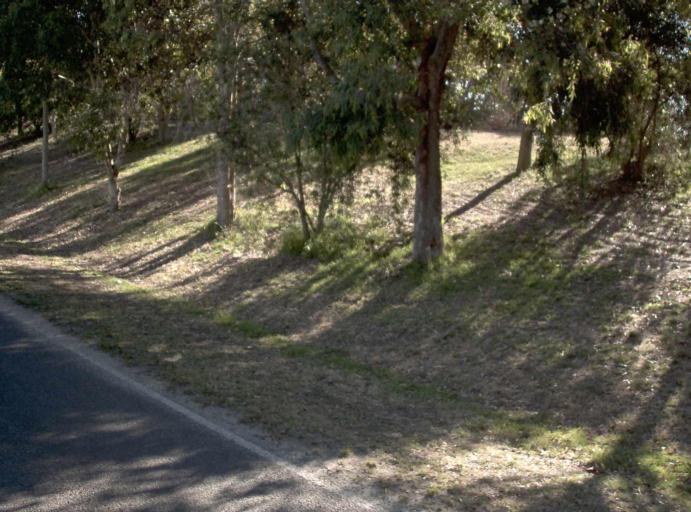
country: AU
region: Victoria
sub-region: Latrobe
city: Morwell
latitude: -38.7087
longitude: 146.3971
